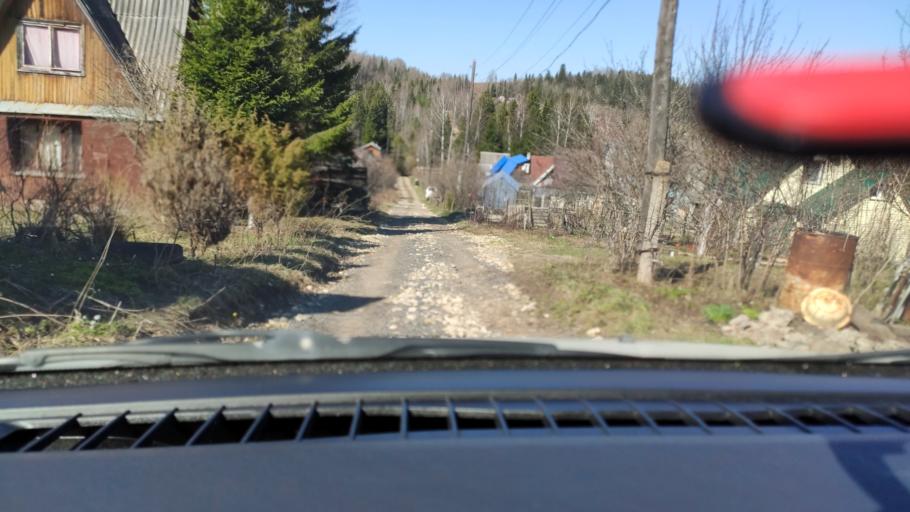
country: RU
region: Perm
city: Bershet'
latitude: 57.7218
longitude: 56.4114
